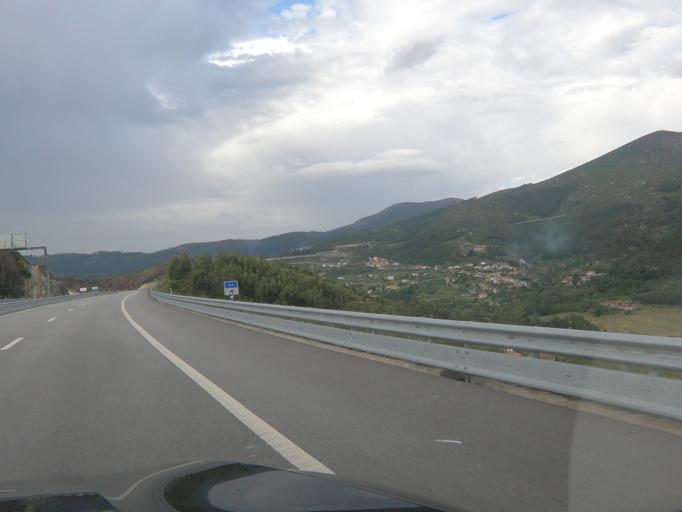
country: PT
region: Porto
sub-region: Amarante
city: Amarante
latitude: 41.2531
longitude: -7.9969
